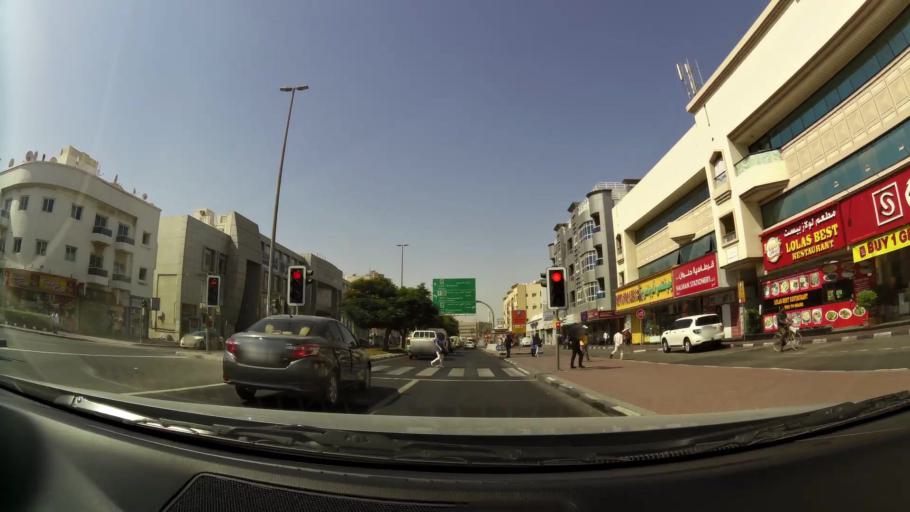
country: AE
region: Ash Shariqah
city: Sharjah
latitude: 25.2378
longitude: 55.2798
